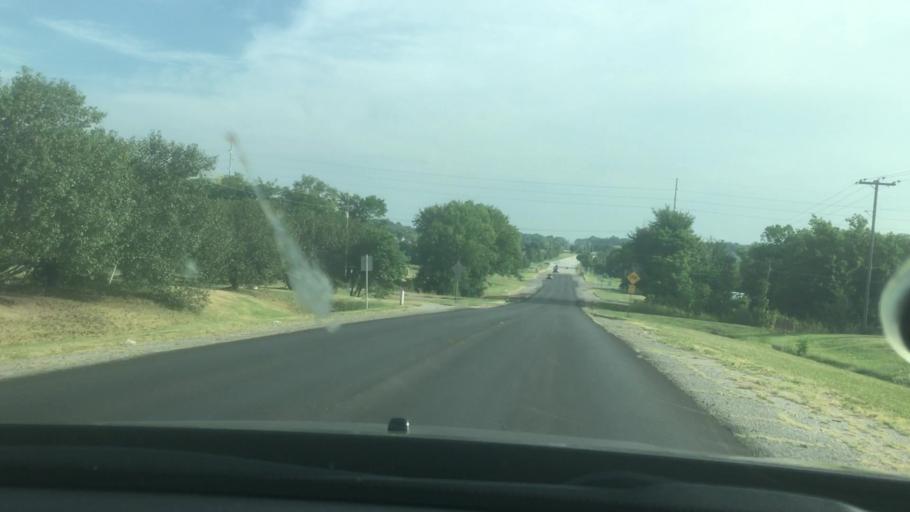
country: US
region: Oklahoma
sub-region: Pontotoc County
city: Ada
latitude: 34.7490
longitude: -96.6701
